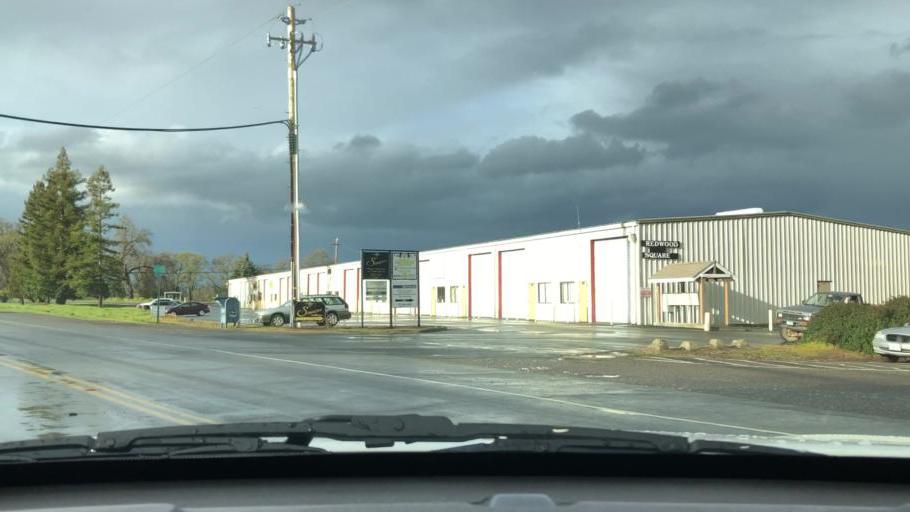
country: US
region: California
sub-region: Mendocino County
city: Talmage
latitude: 39.1104
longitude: -123.1970
